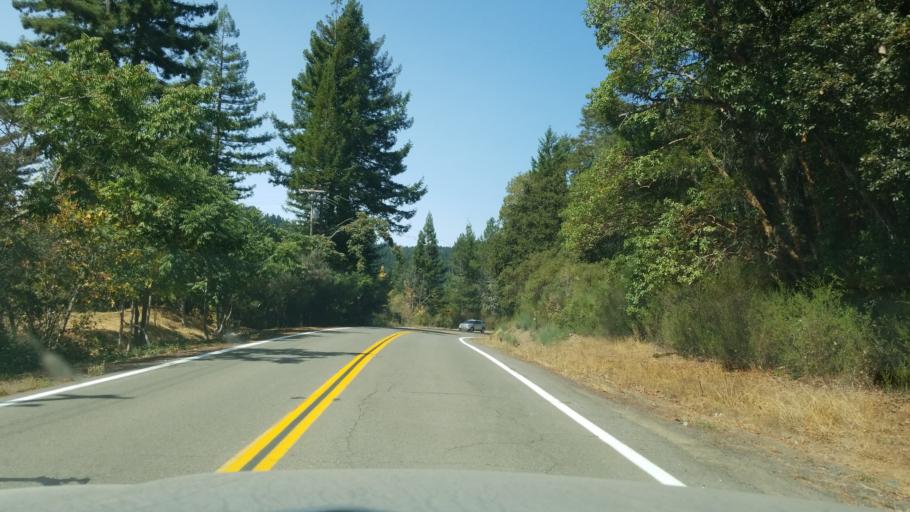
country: US
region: California
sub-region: Mendocino County
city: Laytonville
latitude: 39.8513
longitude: -123.7173
